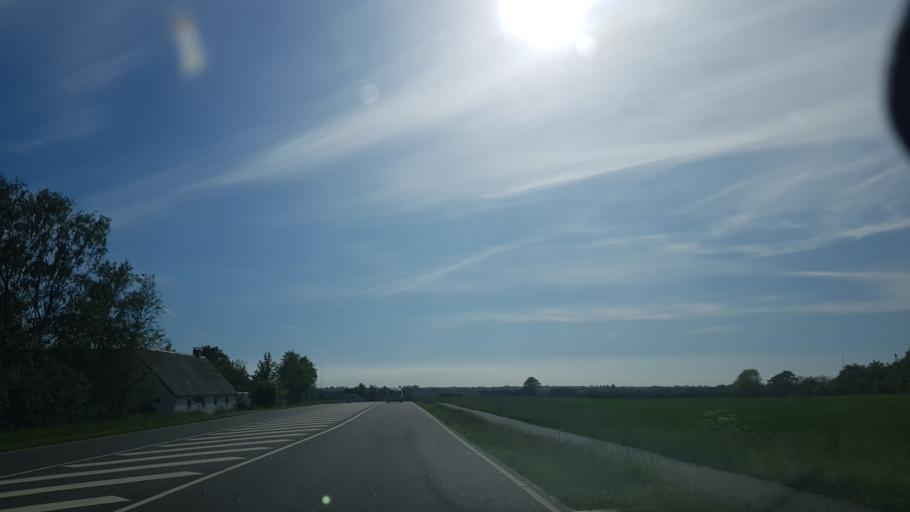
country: DK
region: Zealand
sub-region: Soro Kommune
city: Soro
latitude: 55.4314
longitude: 11.4771
